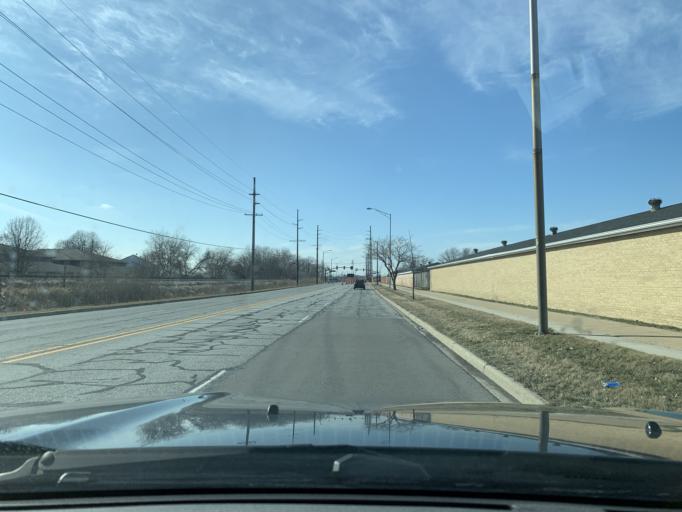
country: US
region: Indiana
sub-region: Lake County
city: Munster
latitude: 41.5387
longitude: -87.4972
